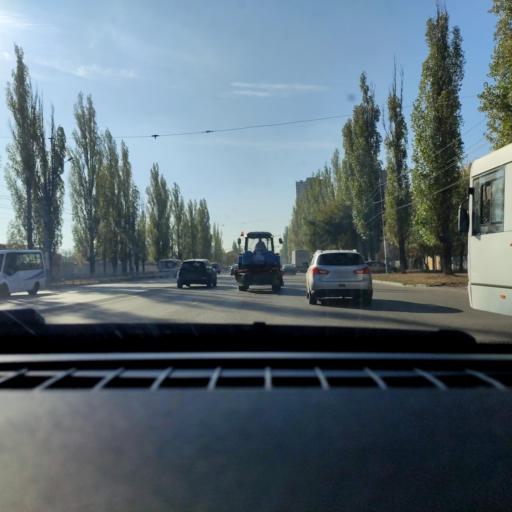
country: RU
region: Voronezj
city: Somovo
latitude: 51.7071
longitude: 39.2764
